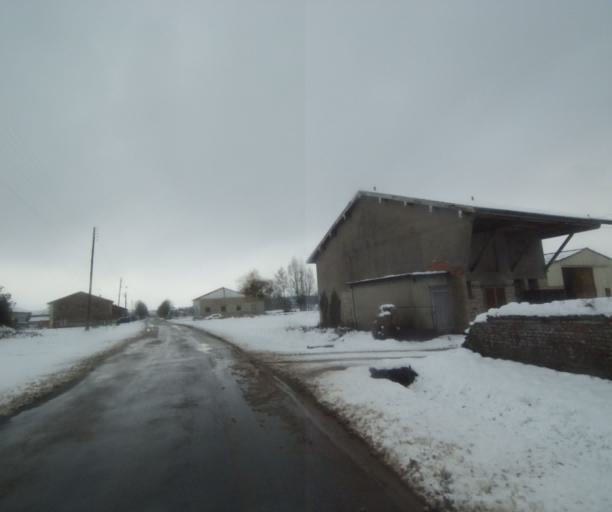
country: FR
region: Champagne-Ardenne
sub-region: Departement de la Haute-Marne
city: Montier-en-Der
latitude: 48.4733
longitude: 4.7864
